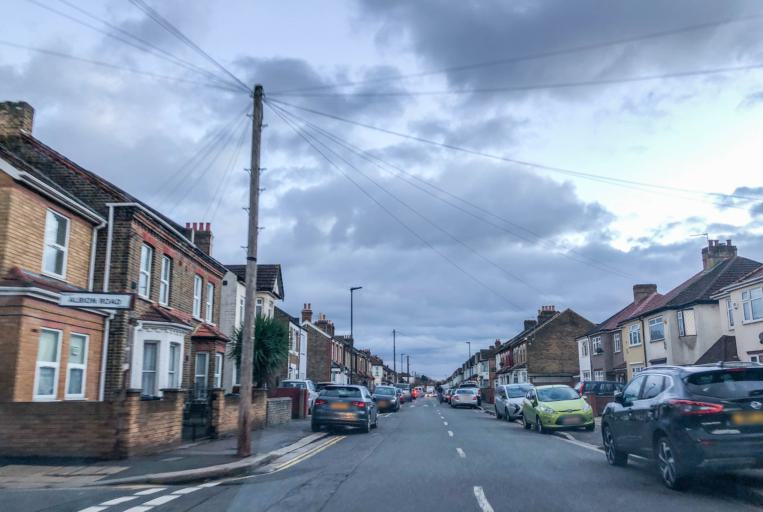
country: GB
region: England
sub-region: Greater London
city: Hounslow
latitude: 51.4629
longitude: -0.3723
